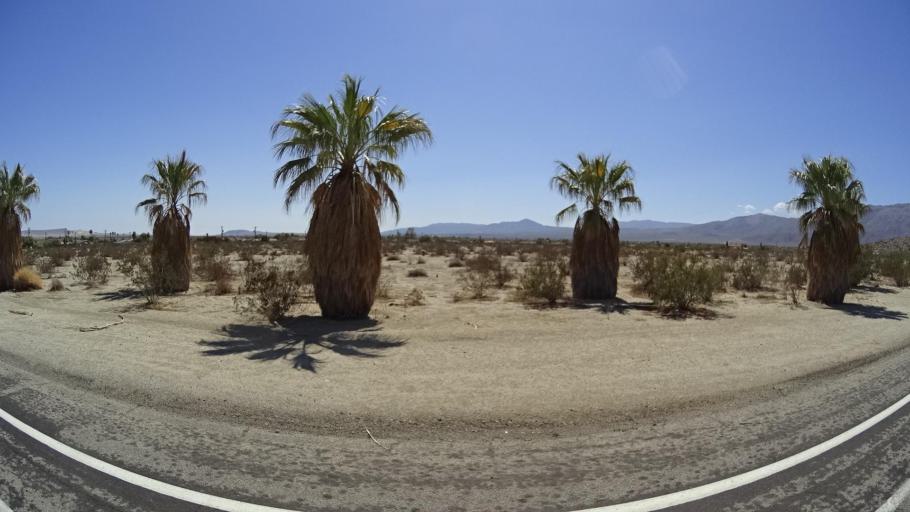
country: US
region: California
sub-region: San Diego County
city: Borrego Springs
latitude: 33.2551
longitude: -116.3772
